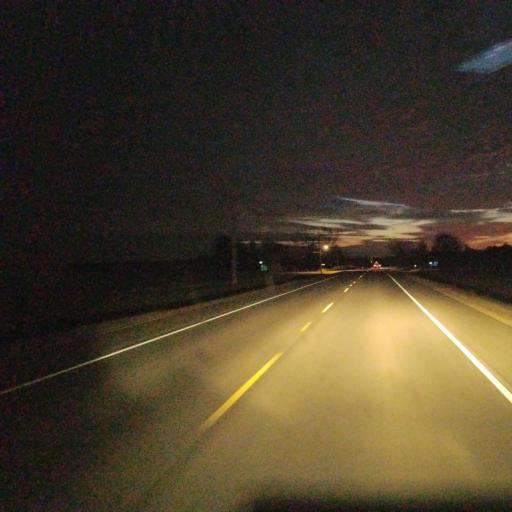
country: US
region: Illinois
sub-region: Fulton County
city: Farmington
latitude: 40.6980
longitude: -89.9194
